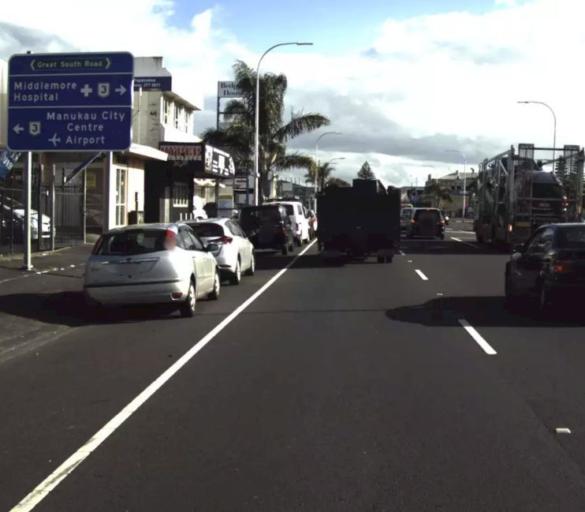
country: NZ
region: Auckland
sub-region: Auckland
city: Wiri
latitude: -36.9675
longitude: 174.8622
